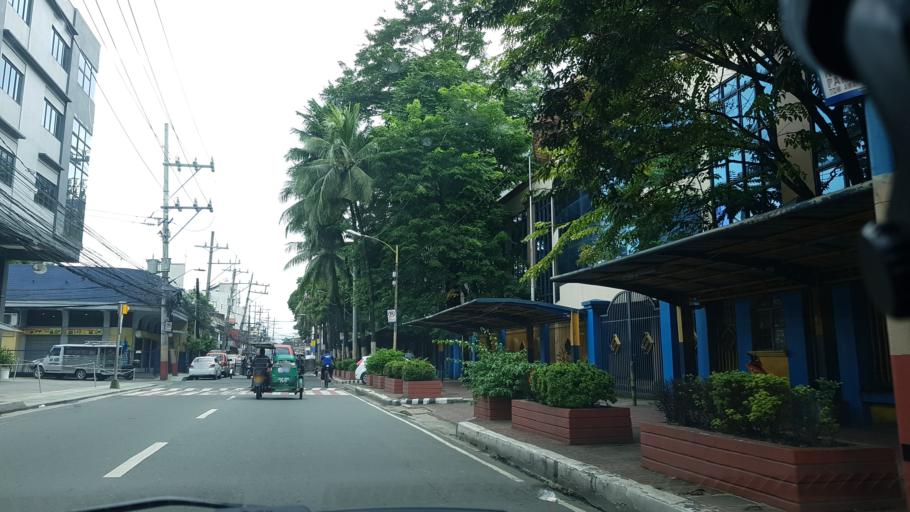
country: PH
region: Metro Manila
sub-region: Pasig
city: Pasig City
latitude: 14.5678
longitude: 121.0764
